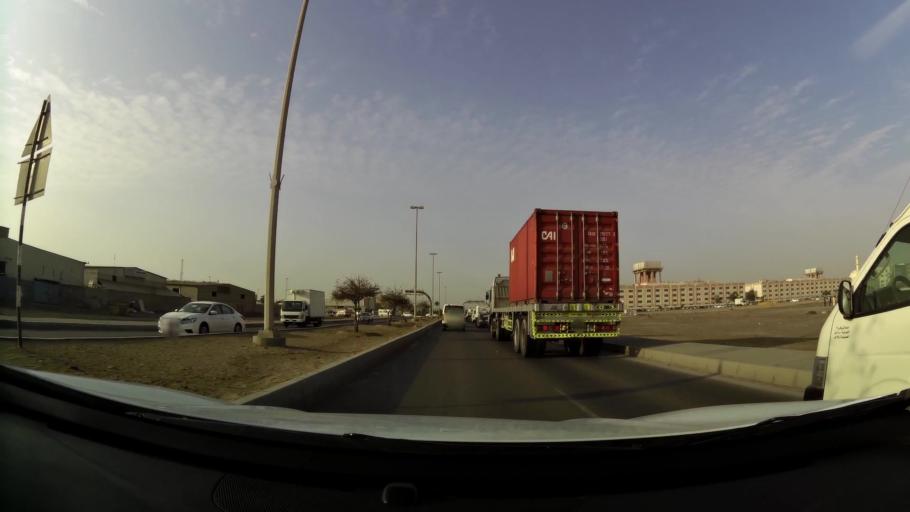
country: AE
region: Abu Dhabi
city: Abu Dhabi
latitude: 24.3582
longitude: 54.5167
